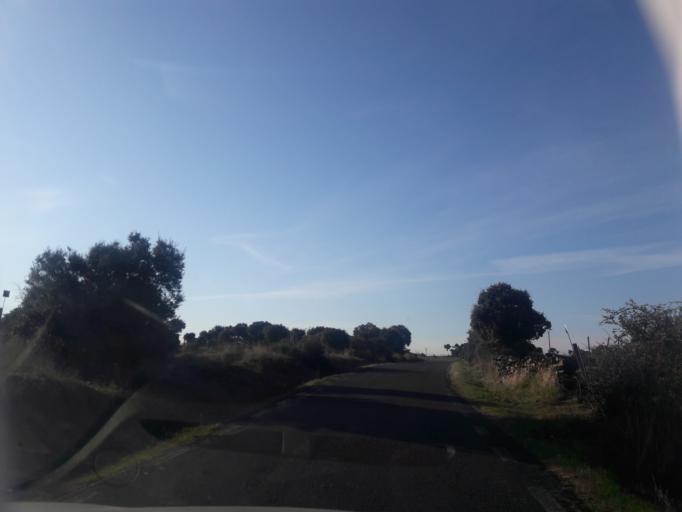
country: ES
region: Castille and Leon
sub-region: Provincia de Salamanca
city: Montejo
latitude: 40.6150
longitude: -5.6067
